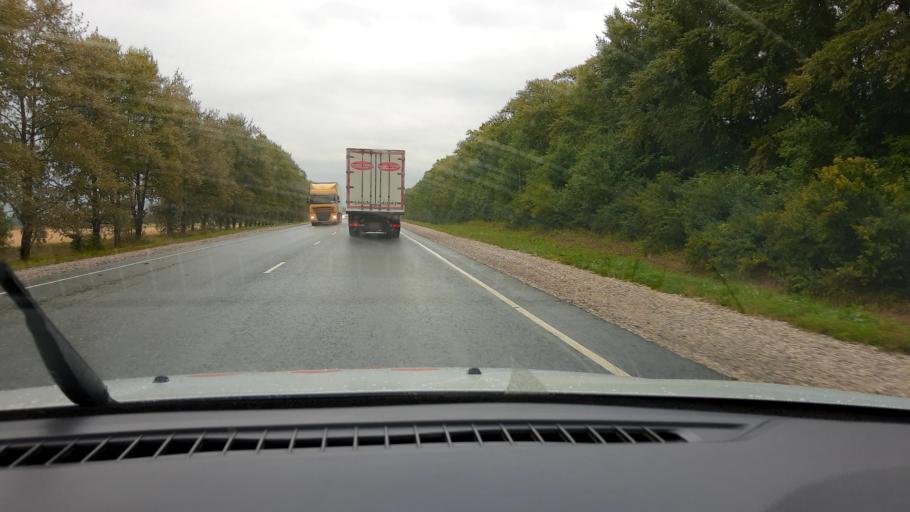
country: RU
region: Chuvashia
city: Yantikovo
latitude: 55.7892
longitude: 47.7172
